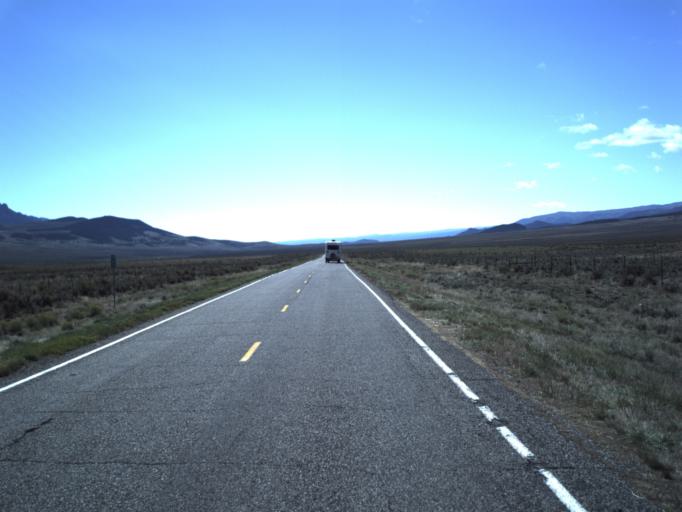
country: US
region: Utah
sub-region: Wayne County
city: Loa
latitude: 38.4206
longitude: -111.9232
